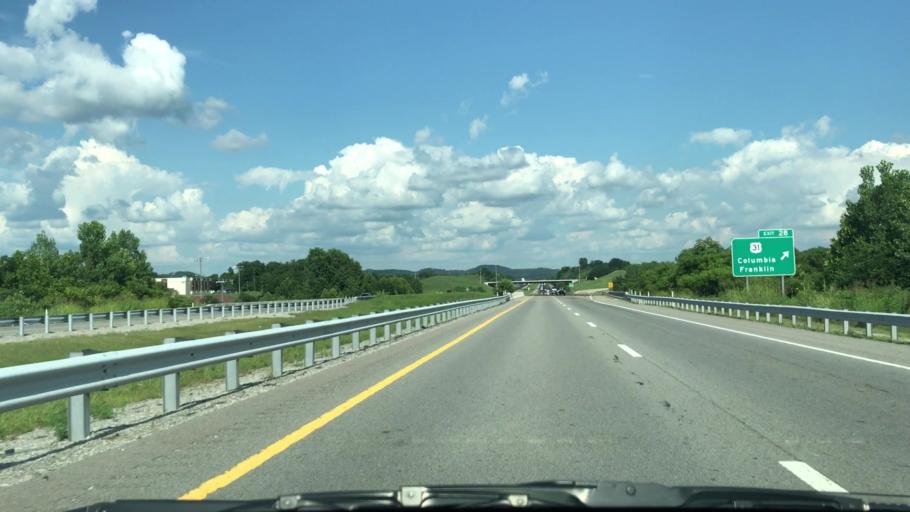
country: US
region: Tennessee
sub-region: Williamson County
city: Thompson's Station
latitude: 35.8225
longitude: -86.8969
